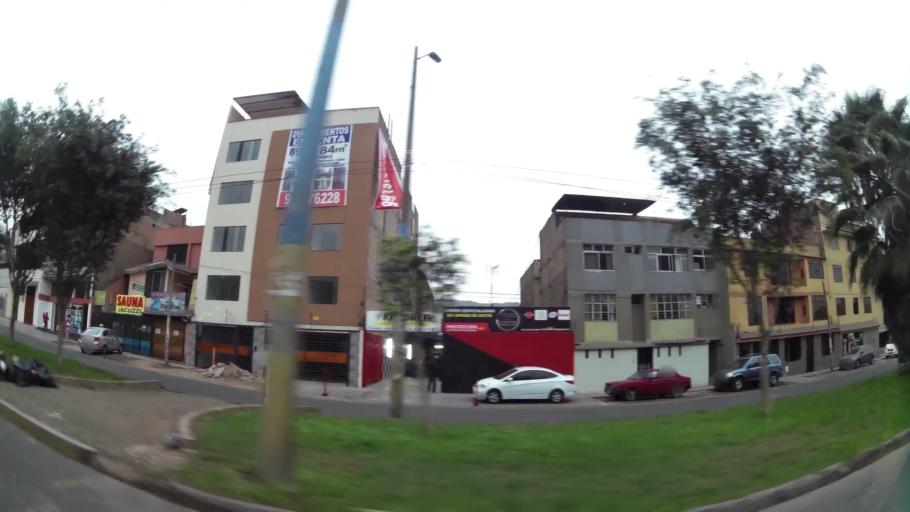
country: PE
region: Lima
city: Lima
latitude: -12.0135
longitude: -76.9859
